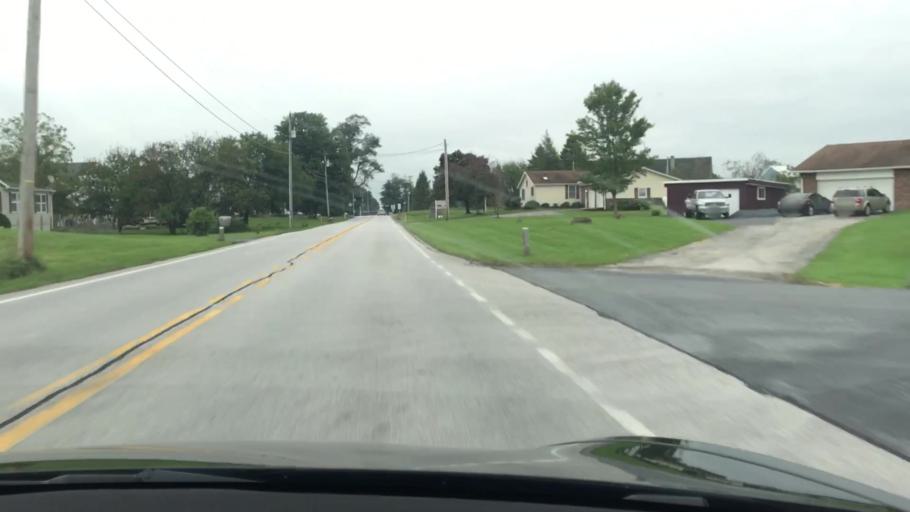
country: US
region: Pennsylvania
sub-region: Adams County
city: Lake Meade
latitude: 39.9408
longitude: -77.0687
